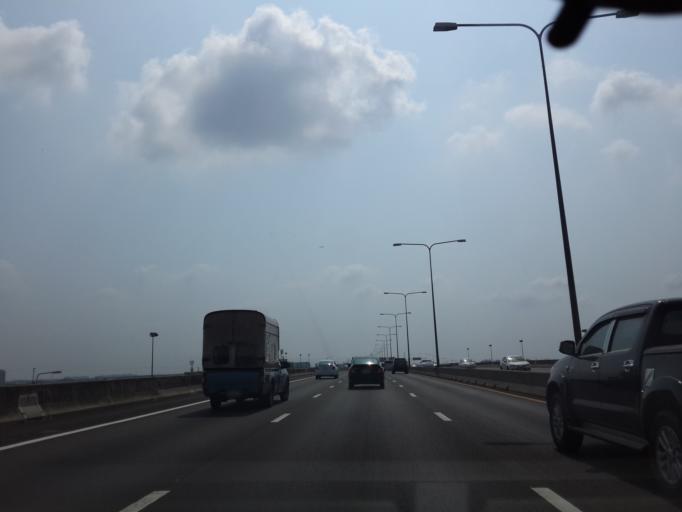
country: TH
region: Bangkok
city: Bang Na
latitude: 13.6304
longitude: 100.7176
